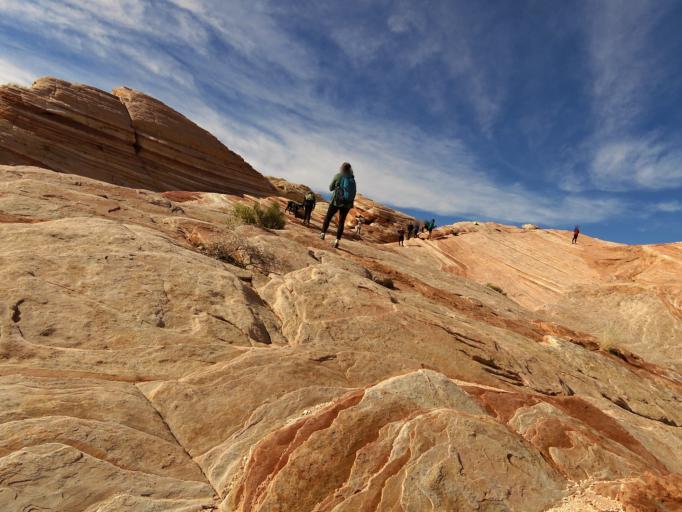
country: US
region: Nevada
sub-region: Clark County
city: Moapa Valley
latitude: 36.4826
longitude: -114.5221
